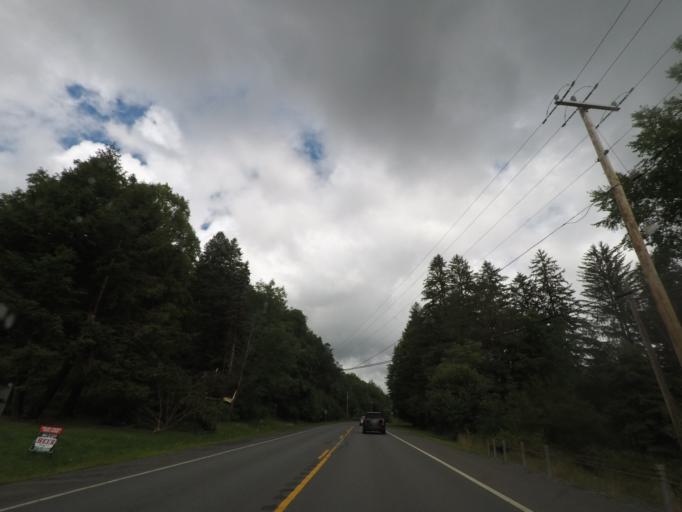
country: US
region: Massachusetts
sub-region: Berkshire County
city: Williamstown
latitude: 42.6755
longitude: -73.3678
